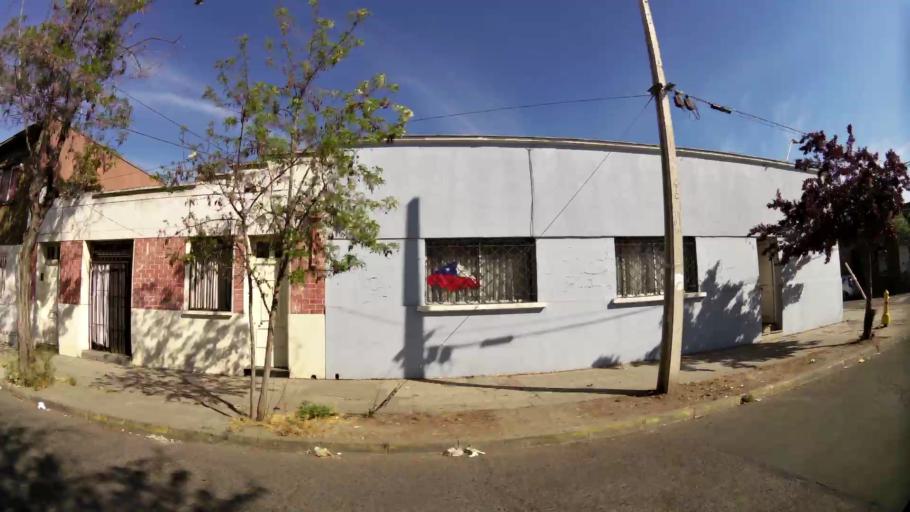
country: CL
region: Santiago Metropolitan
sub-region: Provincia de Santiago
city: Santiago
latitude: -33.4081
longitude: -70.6369
